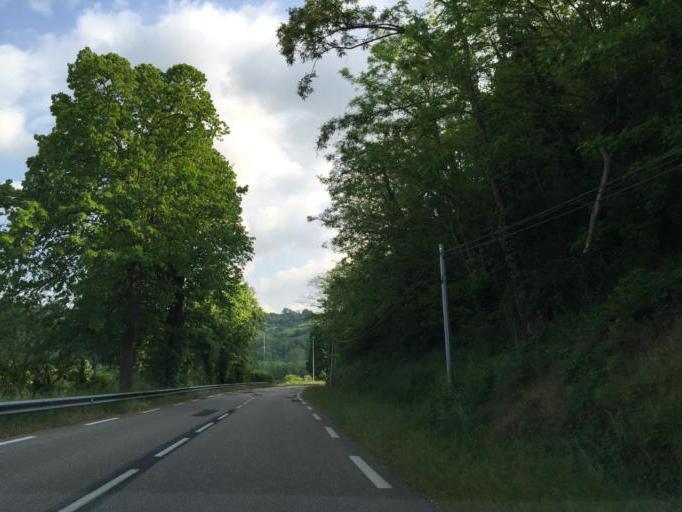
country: FR
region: Rhone-Alpes
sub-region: Departement du Rhone
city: Echalas
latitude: 45.5544
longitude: 4.6813
